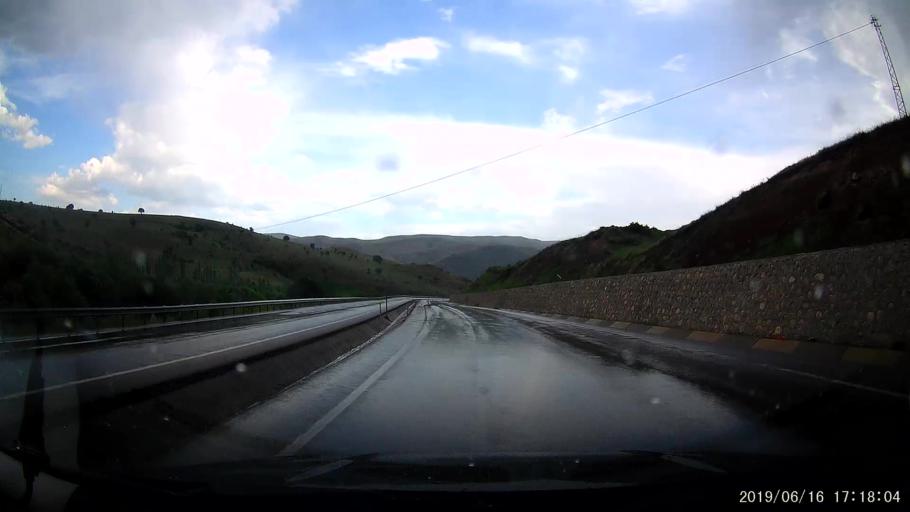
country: TR
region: Erzincan
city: Tercan
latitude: 39.8189
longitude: 40.5285
